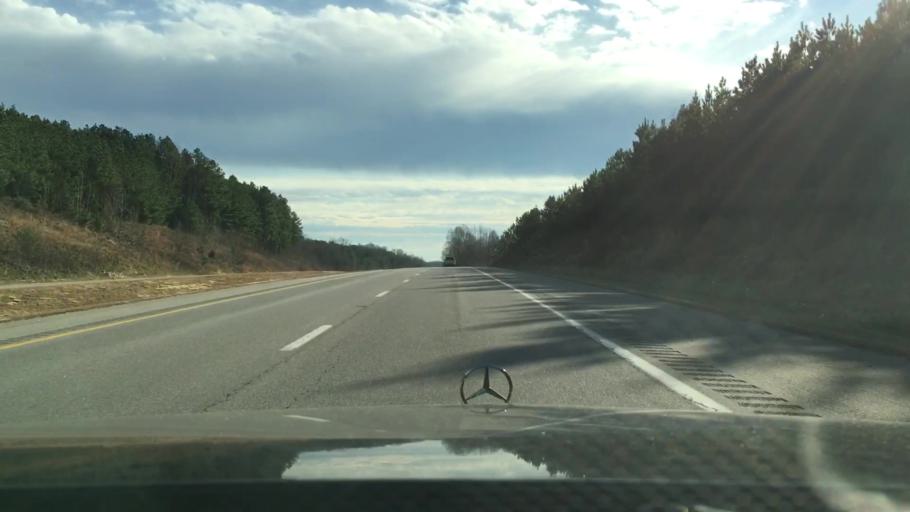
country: US
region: Virginia
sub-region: City of Danville
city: Danville
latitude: 36.6400
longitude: -79.3648
